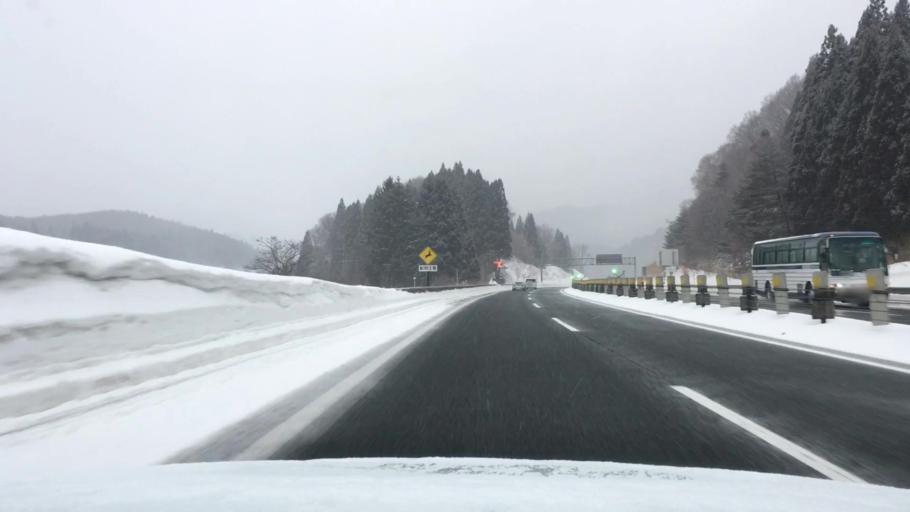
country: JP
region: Akita
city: Hanawa
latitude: 40.1108
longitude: 141.0374
